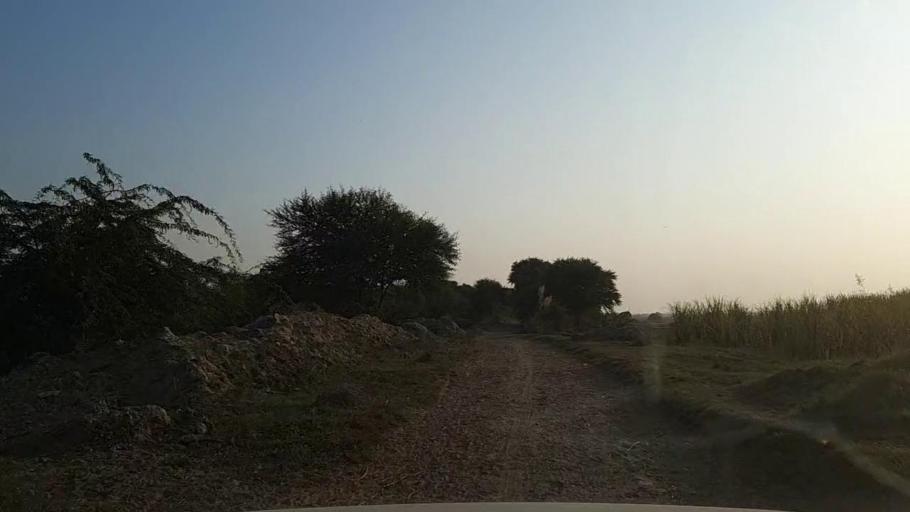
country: PK
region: Sindh
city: Daro Mehar
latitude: 24.7370
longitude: 68.1822
